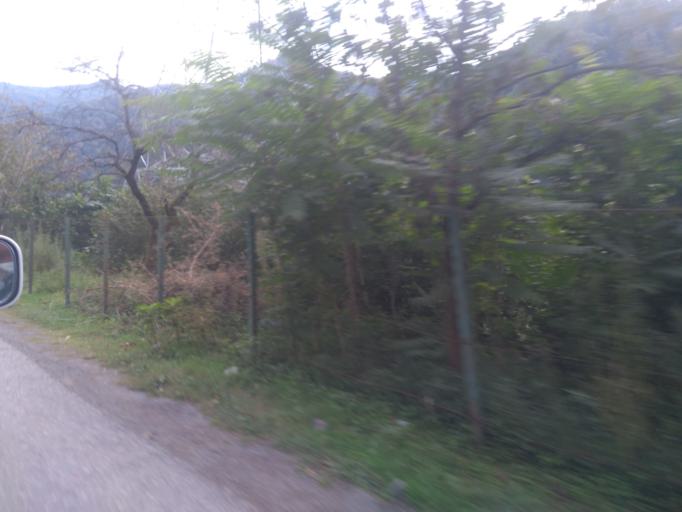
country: TR
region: Artvin
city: Muratli
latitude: 41.5463
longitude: 41.7625
